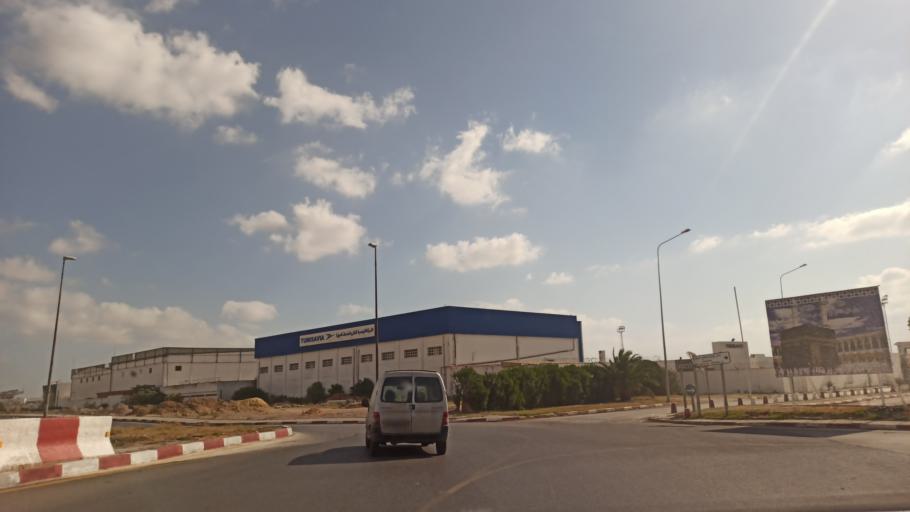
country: TN
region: Ariana
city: Ariana
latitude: 36.8406
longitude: 10.2145
